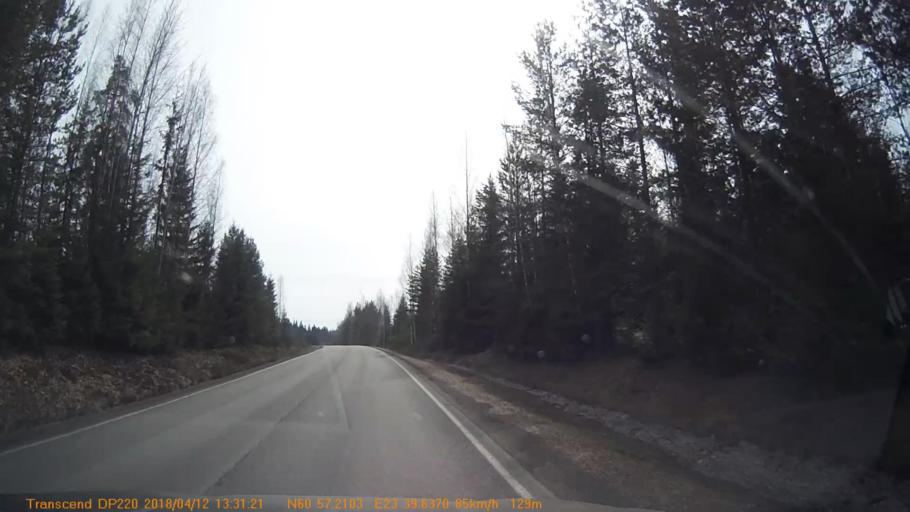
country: FI
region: Haeme
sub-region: Forssa
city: Forssa
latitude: 60.9535
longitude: 23.6606
